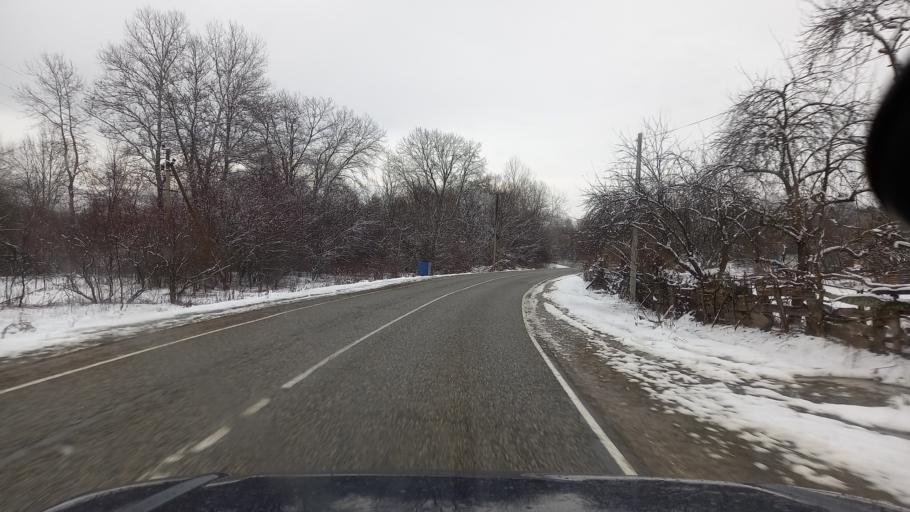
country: RU
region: Adygeya
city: Abadzekhskaya
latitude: 44.3599
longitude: 40.2929
